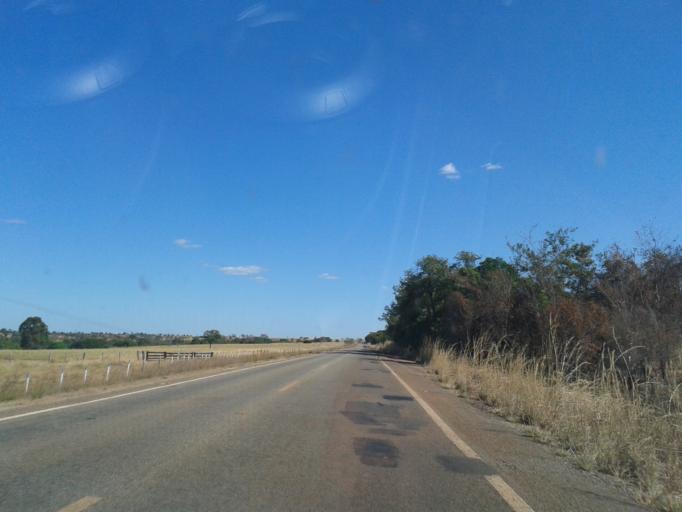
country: BR
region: Goias
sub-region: Mozarlandia
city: Mozarlandia
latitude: -14.3672
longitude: -50.4291
